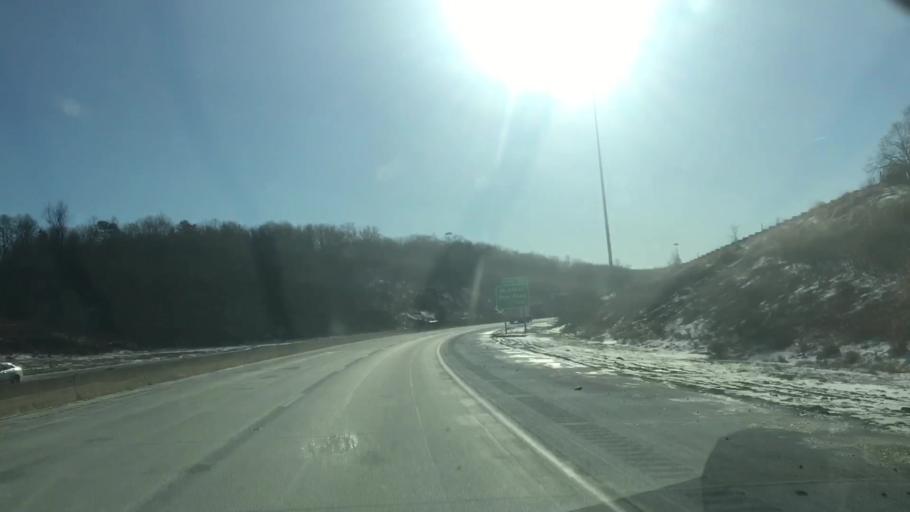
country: US
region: Pennsylvania
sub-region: Allegheny County
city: Enlow
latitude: 40.4654
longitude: -80.1993
